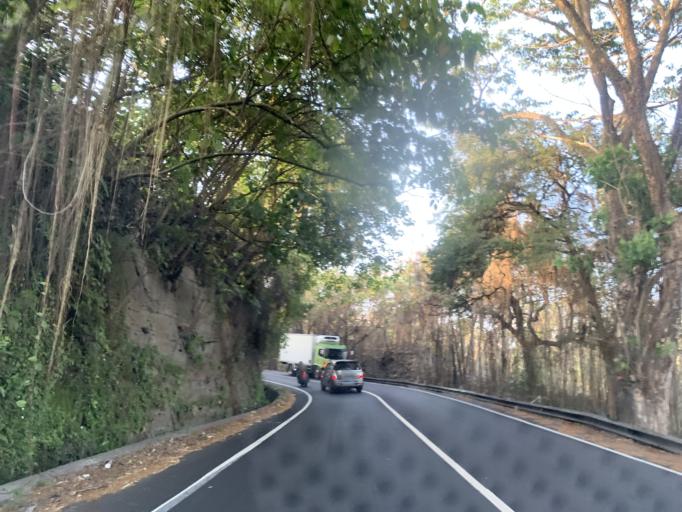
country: ID
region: Bali
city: Banjar Delodrurung
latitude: -8.4974
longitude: 114.9668
